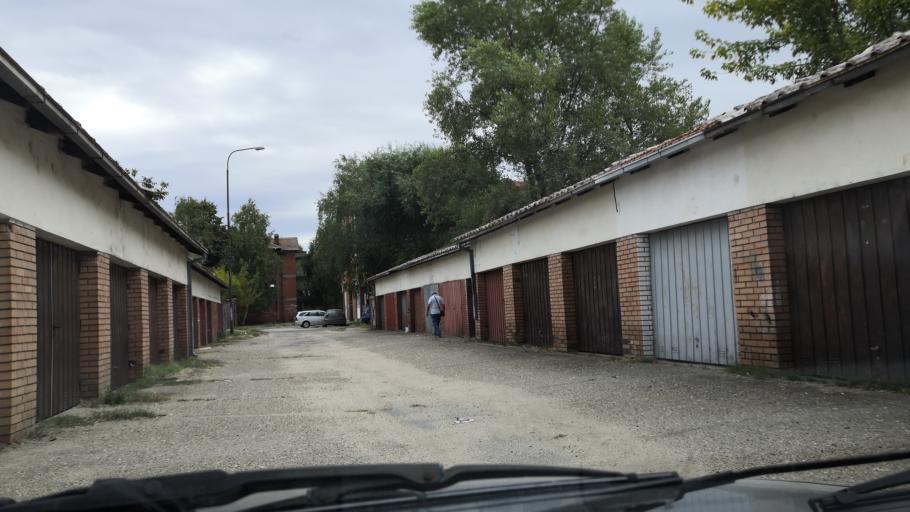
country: RS
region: Central Serbia
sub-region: Borski Okrug
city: Negotin
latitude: 44.2278
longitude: 22.5191
